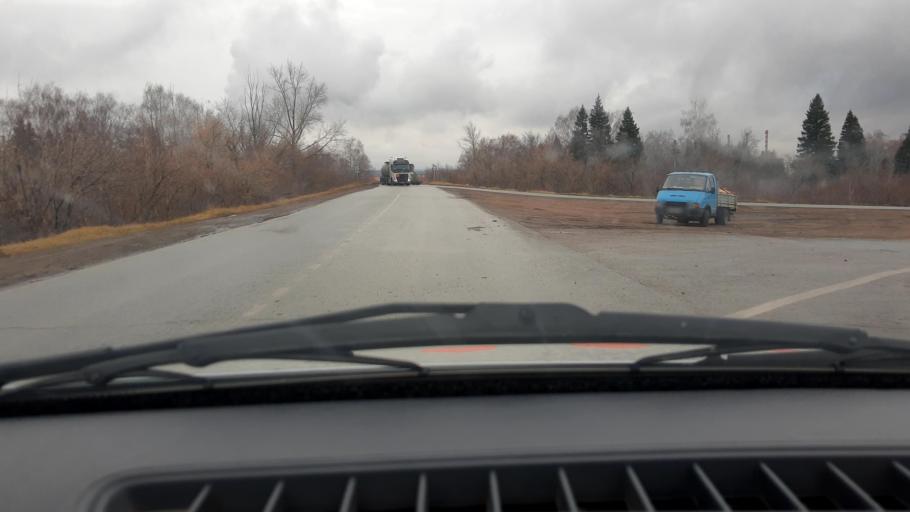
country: RU
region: Bashkortostan
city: Iglino
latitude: 54.7766
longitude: 56.2549
